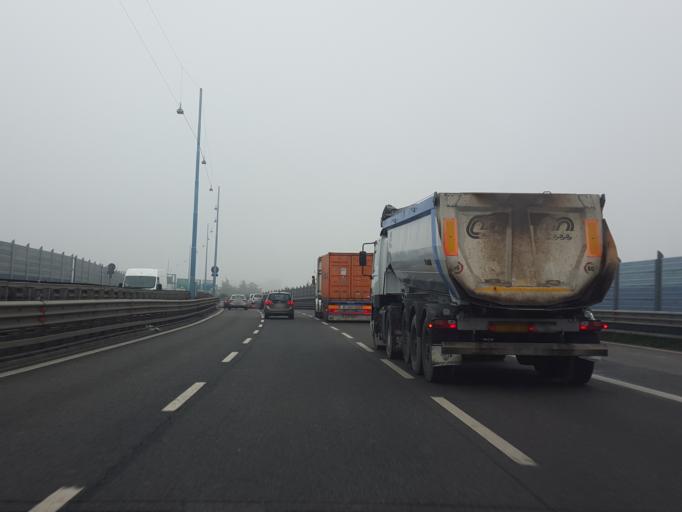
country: IT
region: Veneto
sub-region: Provincia di Venezia
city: Mestre
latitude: 45.4973
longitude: 12.2295
